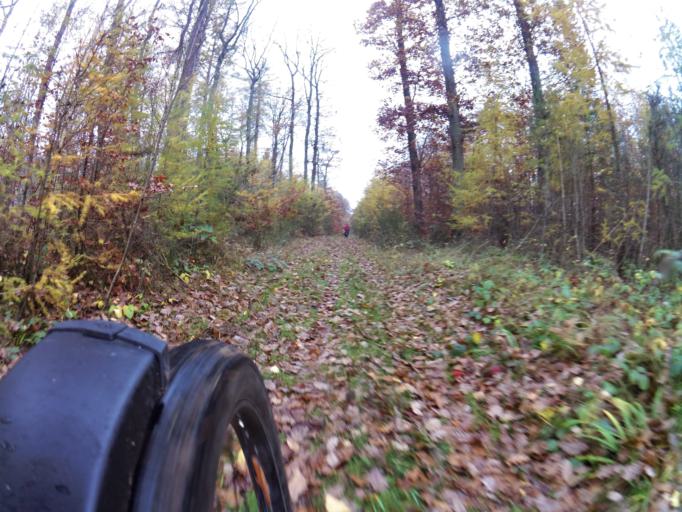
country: PL
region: Pomeranian Voivodeship
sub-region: Powiat pucki
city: Krokowa
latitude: 54.7321
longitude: 18.1316
